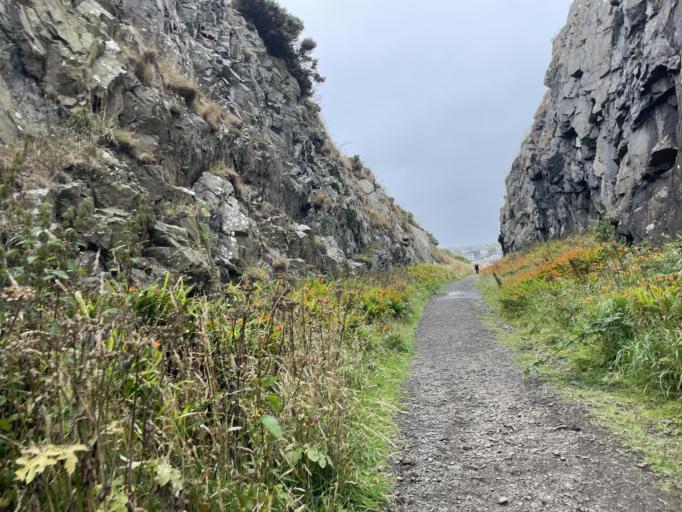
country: GB
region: Scotland
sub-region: Dumfries and Galloway
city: Stranraer
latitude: 54.8382
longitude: -5.1140
